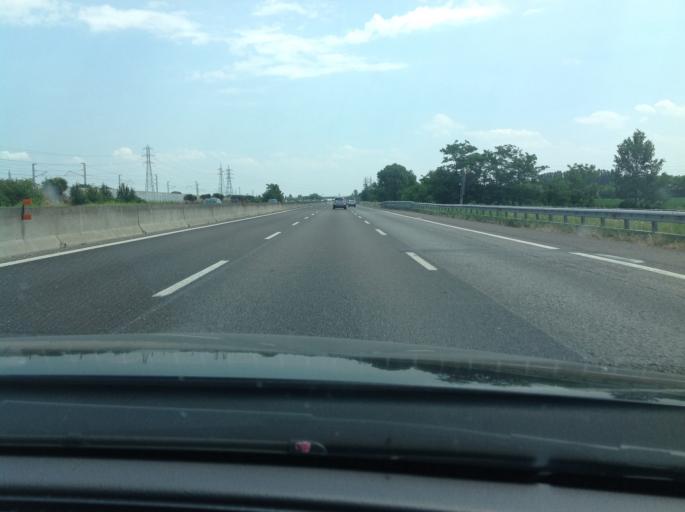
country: IT
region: Lombardy
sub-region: Provincia di Lodi
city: Somaglia
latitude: 45.1556
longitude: 9.6156
